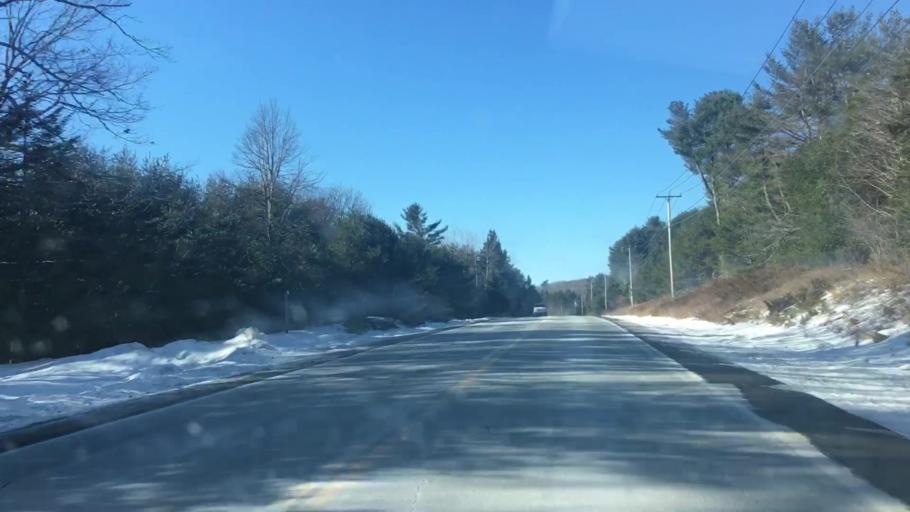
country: US
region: Maine
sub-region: Hancock County
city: Surry
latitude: 44.4958
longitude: -68.4824
